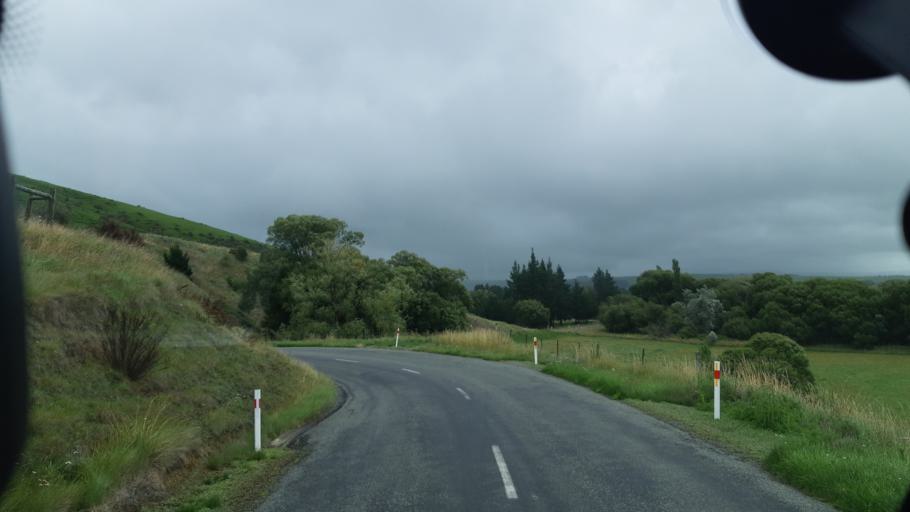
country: NZ
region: Canterbury
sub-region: Timaru District
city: Pleasant Point
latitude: -44.3986
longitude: 171.0043
